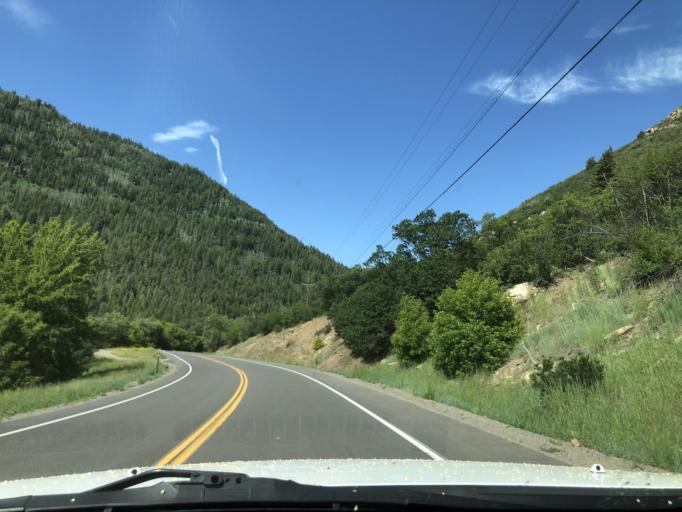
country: US
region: Colorado
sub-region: Delta County
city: Paonia
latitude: 38.9398
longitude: -107.3696
